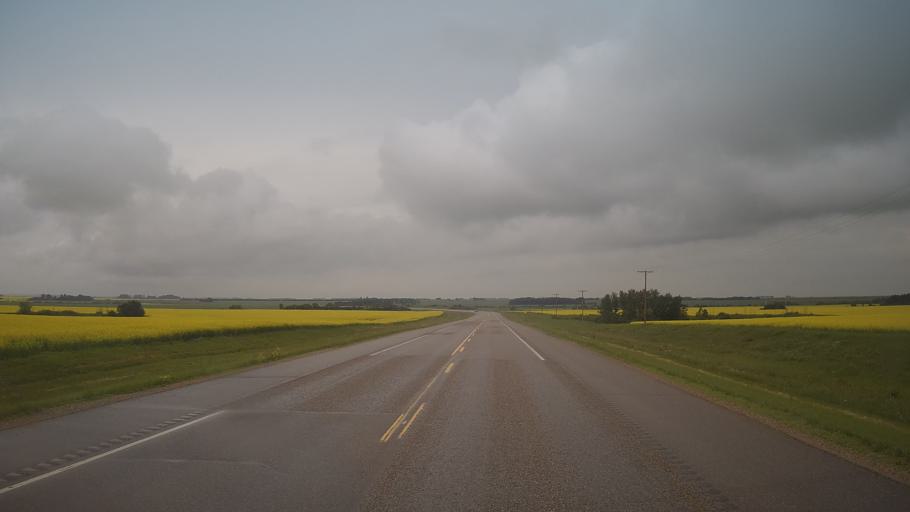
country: CA
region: Saskatchewan
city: Wilkie
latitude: 52.4309
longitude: -108.9201
